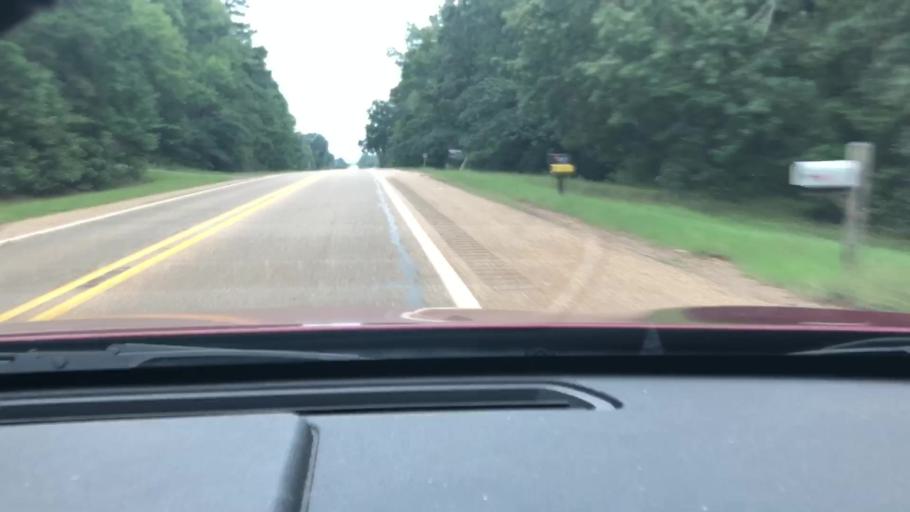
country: US
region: Arkansas
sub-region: Miller County
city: Texarkana
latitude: 33.4293
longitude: -93.9384
